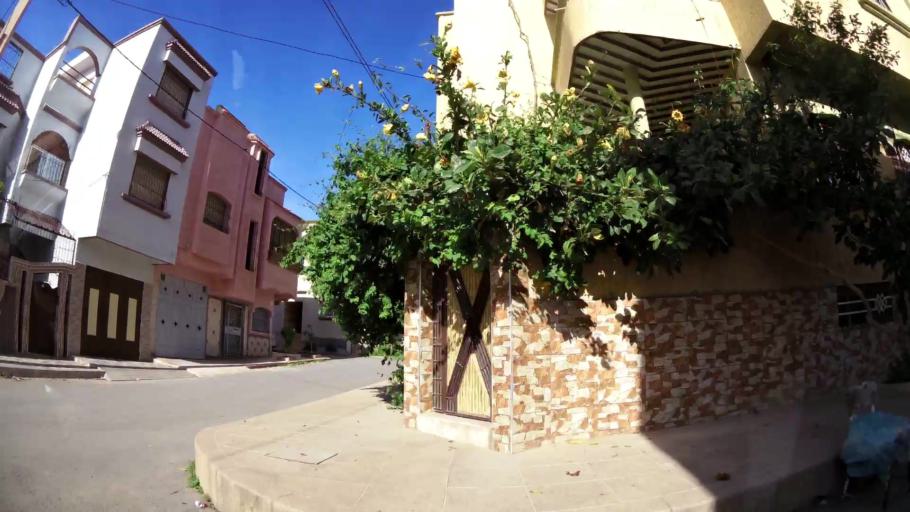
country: MA
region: Oriental
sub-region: Oujda-Angad
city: Oujda
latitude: 34.6671
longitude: -1.8991
